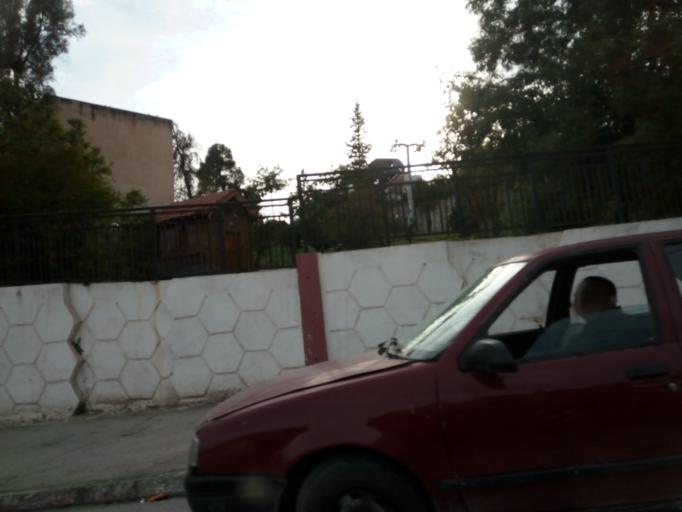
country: DZ
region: Constantine
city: Constantine
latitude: 36.3720
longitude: 6.6198
